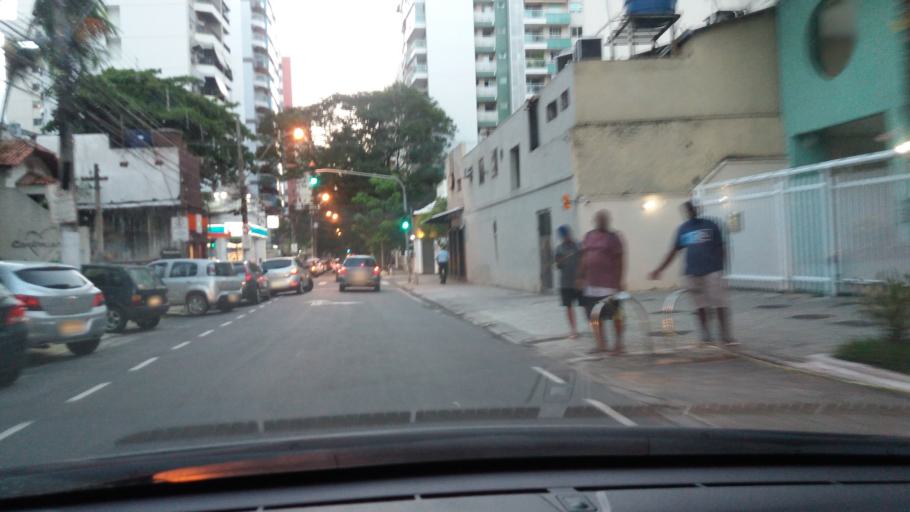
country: BR
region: Rio de Janeiro
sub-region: Niteroi
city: Niteroi
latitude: -22.9017
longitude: -43.1028
